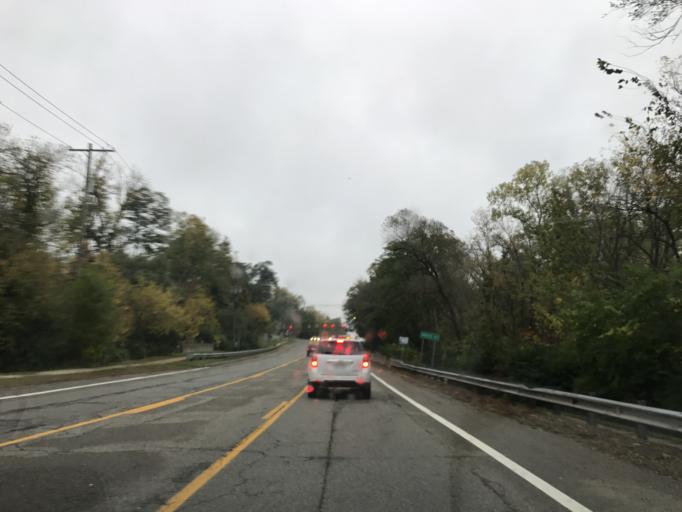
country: US
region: Michigan
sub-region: Oakland County
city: Franklin
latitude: 42.5000
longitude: -83.3222
